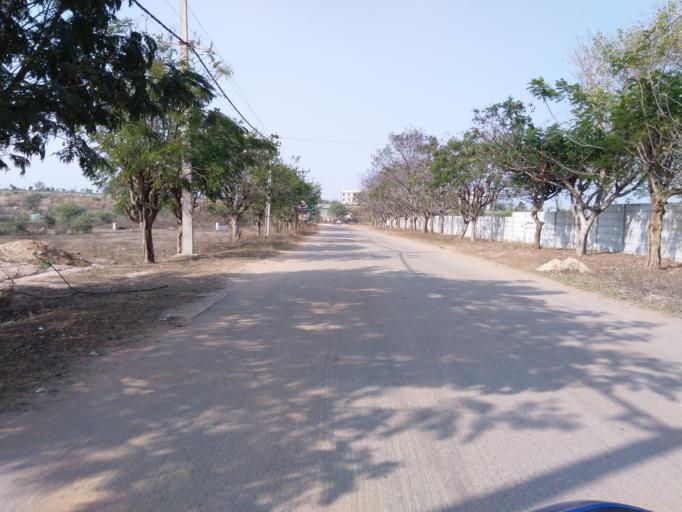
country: IN
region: Telangana
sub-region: Rangareddi
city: Quthbullapur
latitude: 17.5950
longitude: 78.4174
